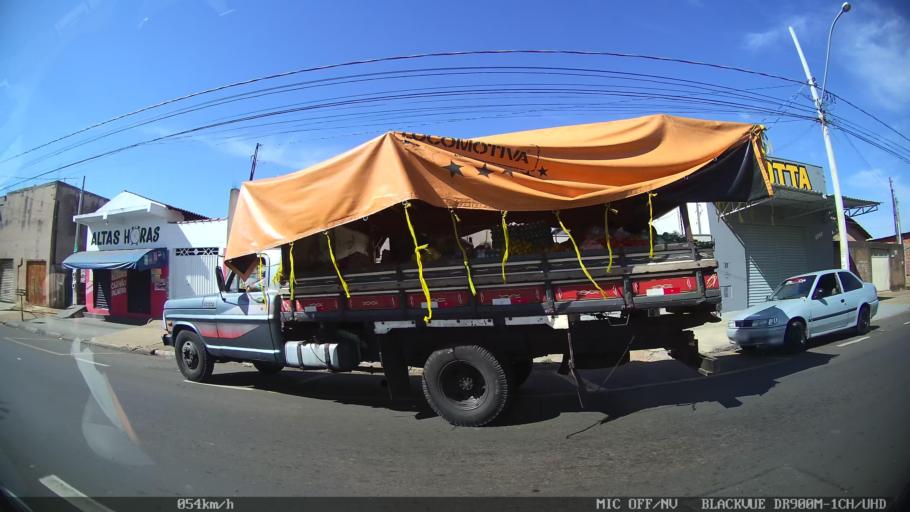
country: BR
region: Sao Paulo
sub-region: Franca
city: Franca
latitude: -20.4979
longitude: -47.3979
